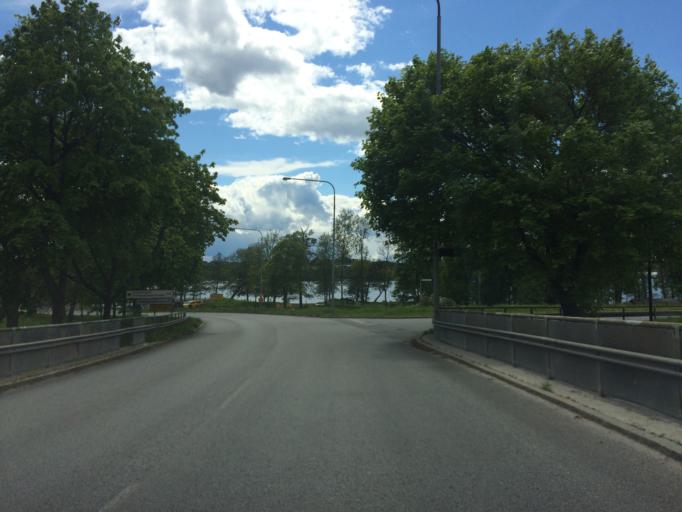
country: SE
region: Stockholm
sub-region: Botkyrka Kommun
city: Fittja
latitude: 59.2632
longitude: 17.8796
